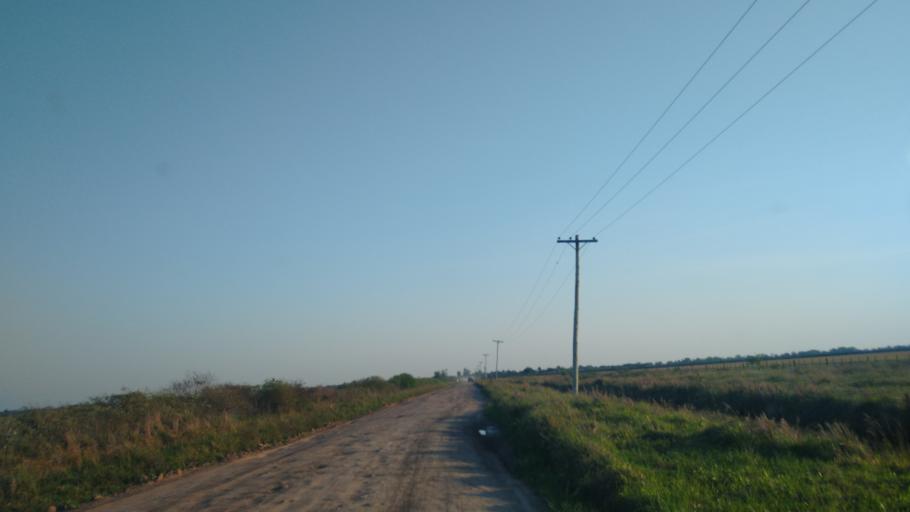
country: PY
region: Neembucu
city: Cerrito
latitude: -27.3871
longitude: -57.6577
